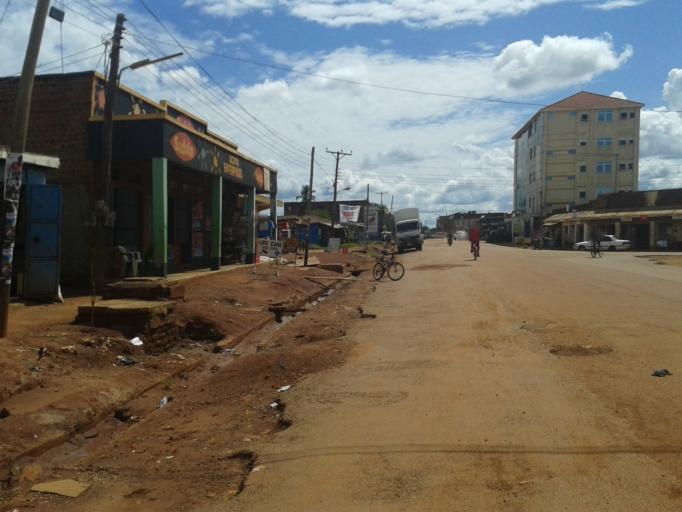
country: UG
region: Northern Region
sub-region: Gulu District
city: Gulu
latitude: 2.7703
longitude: 32.3020
